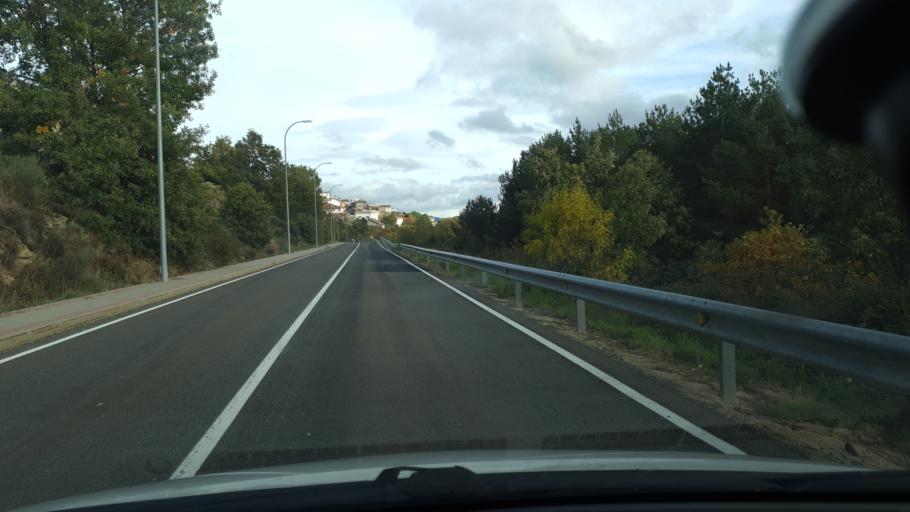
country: ES
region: Castille and Leon
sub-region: Provincia de Avila
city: Hoyocasero
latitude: 40.3995
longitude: -4.9819
